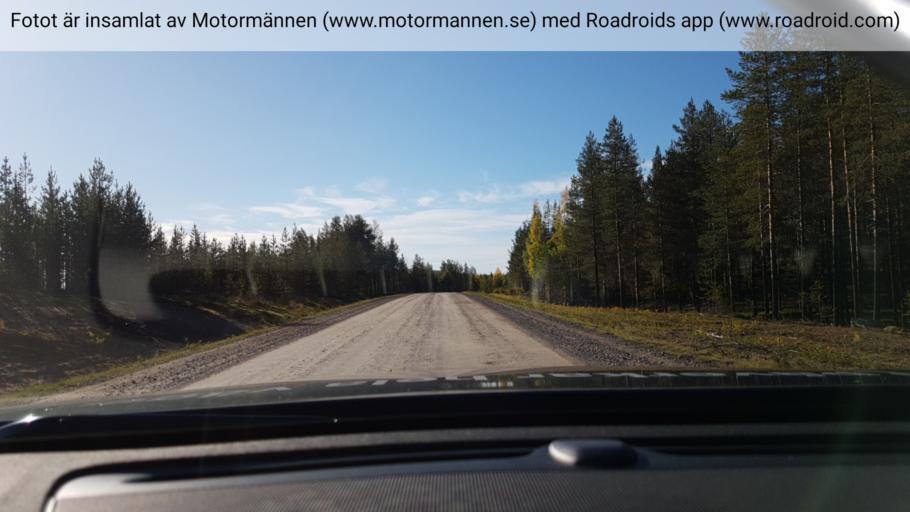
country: SE
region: Norrbotten
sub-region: Alvsbyns Kommun
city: AElvsbyn
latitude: 66.2735
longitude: 21.0895
